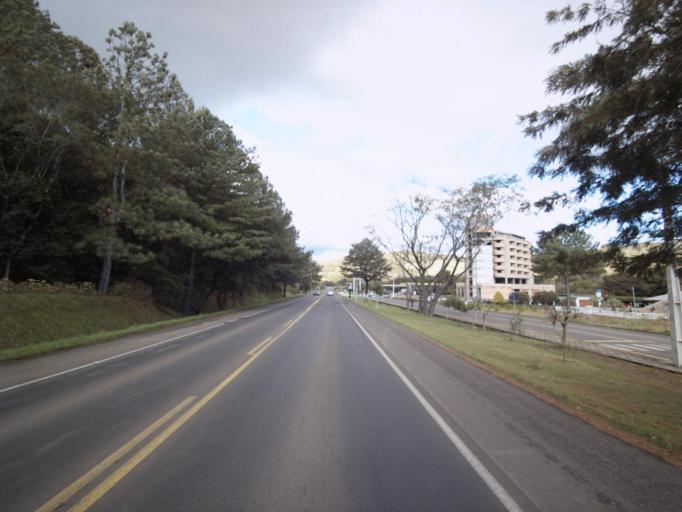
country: BR
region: Santa Catarina
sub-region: Joacaba
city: Joacaba
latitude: -27.2833
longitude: -51.4358
